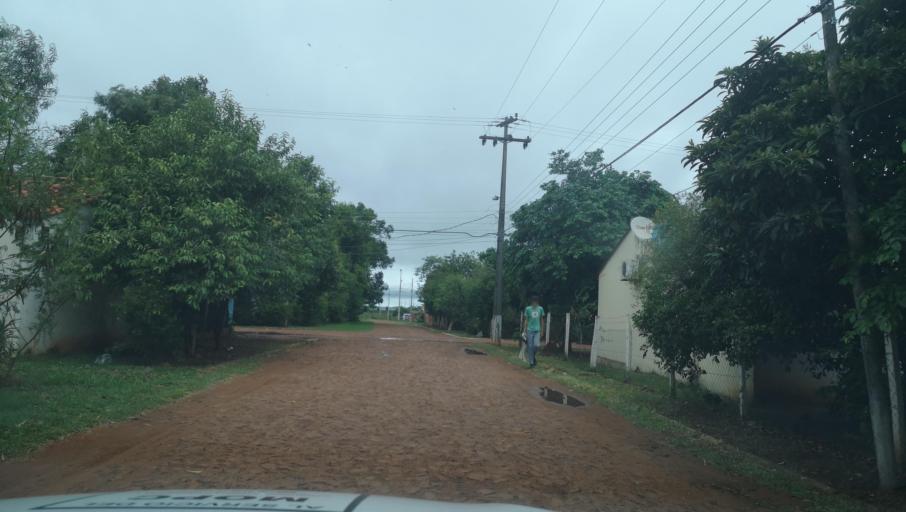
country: PY
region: Misiones
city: Santa Maria
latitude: -26.9009
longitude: -57.0370
